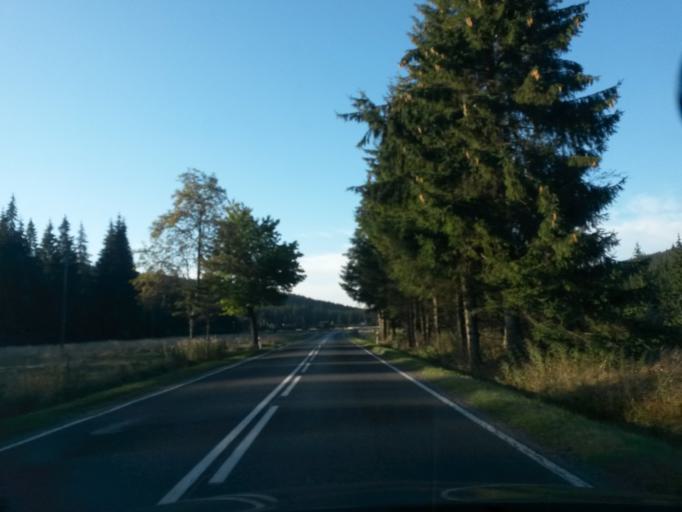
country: PL
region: Lesser Poland Voivodeship
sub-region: Powiat tatrzanski
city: Koscielisko
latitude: 49.2972
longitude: 19.8406
